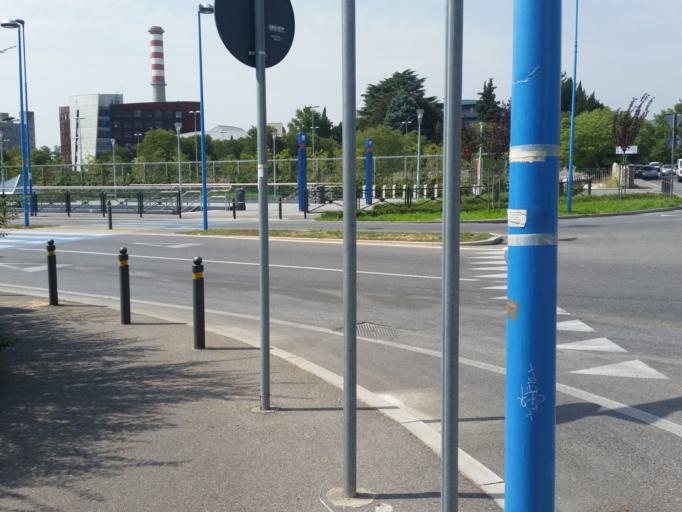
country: IT
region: Lombardy
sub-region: Provincia di Brescia
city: Bovezzo
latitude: 45.5631
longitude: 10.2354
